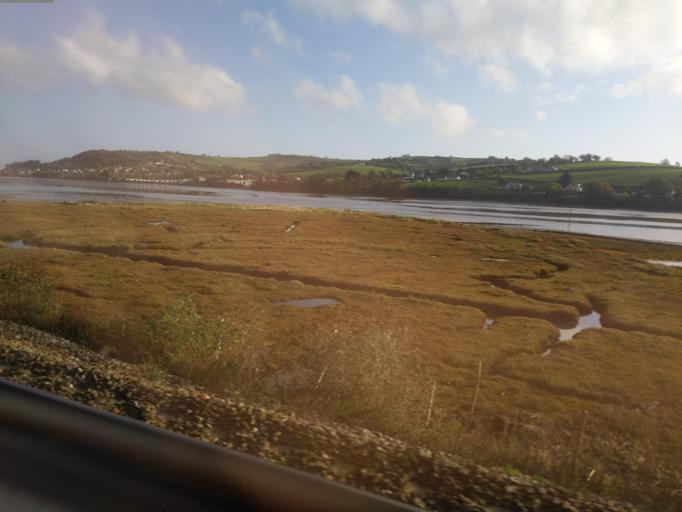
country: GB
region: England
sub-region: Devon
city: Bishopsteignton
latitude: 50.5458
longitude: -3.5391
